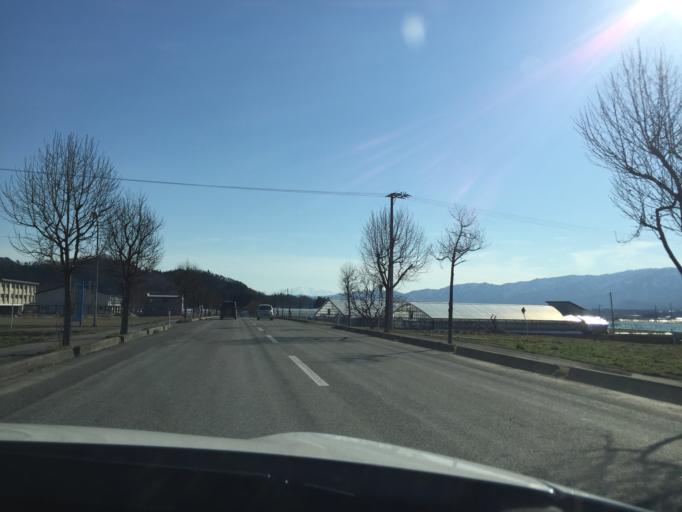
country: JP
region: Yamagata
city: Nagai
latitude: 38.1671
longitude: 140.0856
